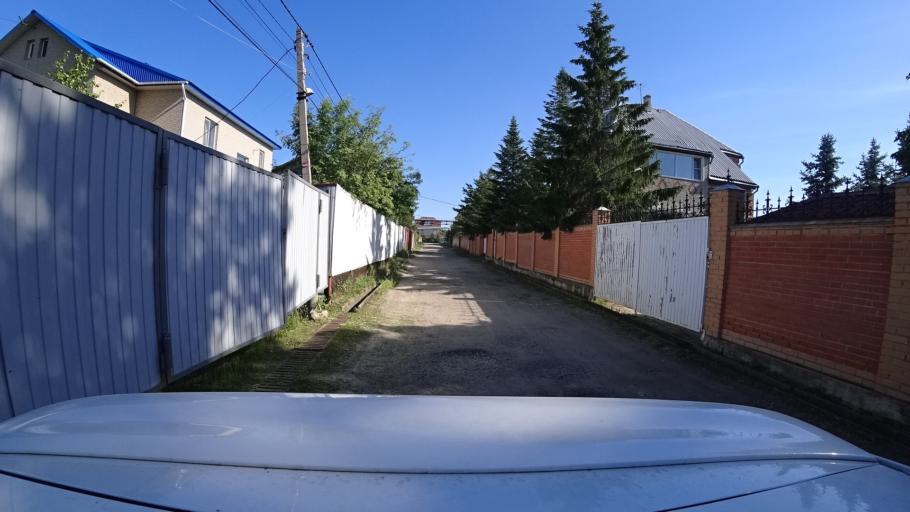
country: RU
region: Khabarovsk Krai
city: Topolevo
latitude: 48.5428
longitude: 135.1777
